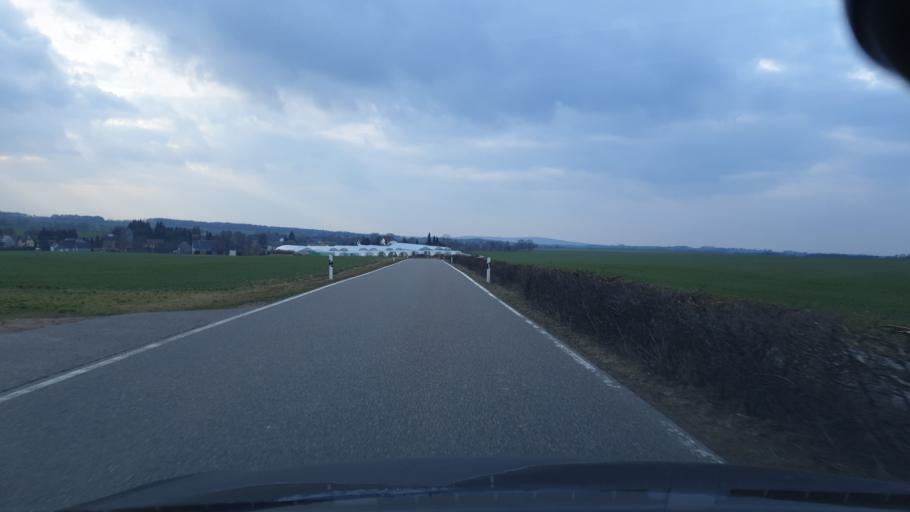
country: DE
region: Saxony
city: Altmittweida
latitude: 50.9870
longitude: 12.9391
